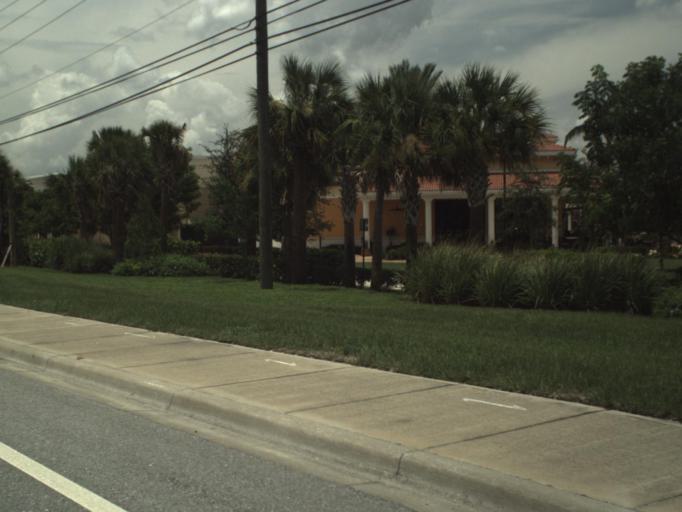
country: US
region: Florida
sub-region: Palm Beach County
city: Villages of Oriole
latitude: 26.4539
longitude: -80.1882
